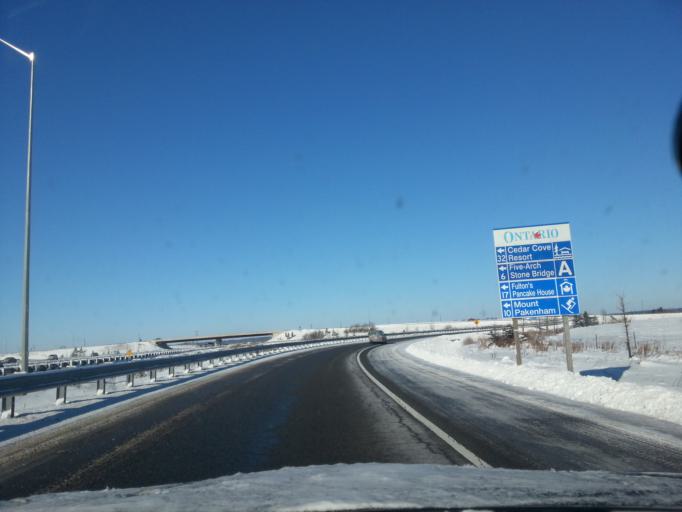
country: CA
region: Ontario
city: Arnprior
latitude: 45.3608
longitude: -76.2308
